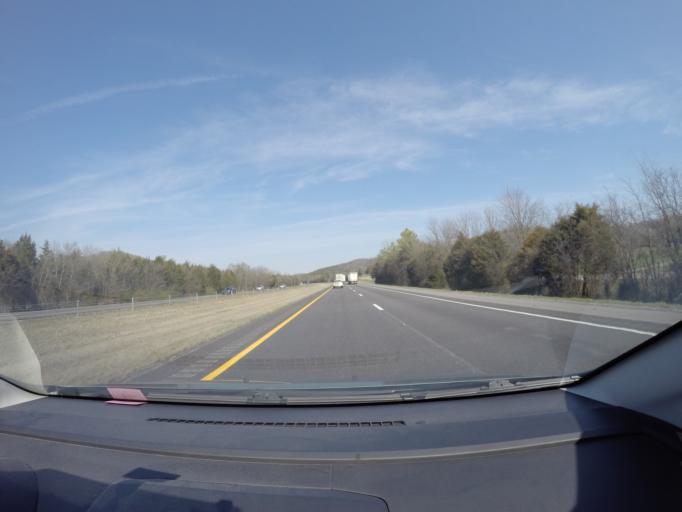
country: US
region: Tennessee
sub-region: Rutherford County
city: Plainview
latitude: 35.6453
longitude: -86.2530
